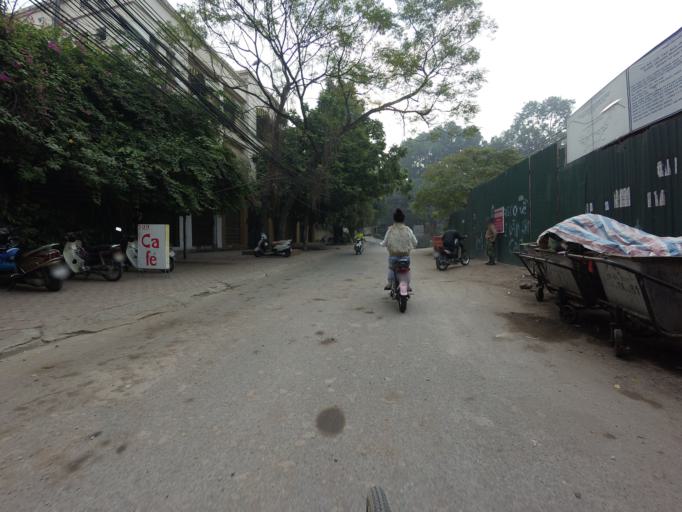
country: VN
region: Ha Noi
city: Hanoi
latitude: 21.0408
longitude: 105.8289
